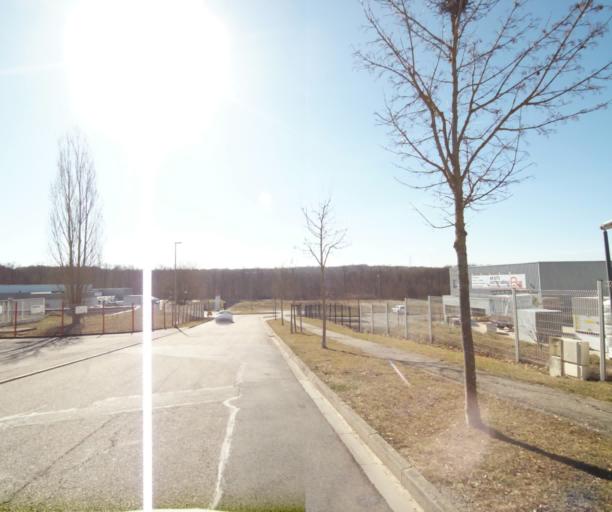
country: FR
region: Lorraine
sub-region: Departement de Meurthe-et-Moselle
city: Richardmenil
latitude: 48.6103
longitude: 6.1818
